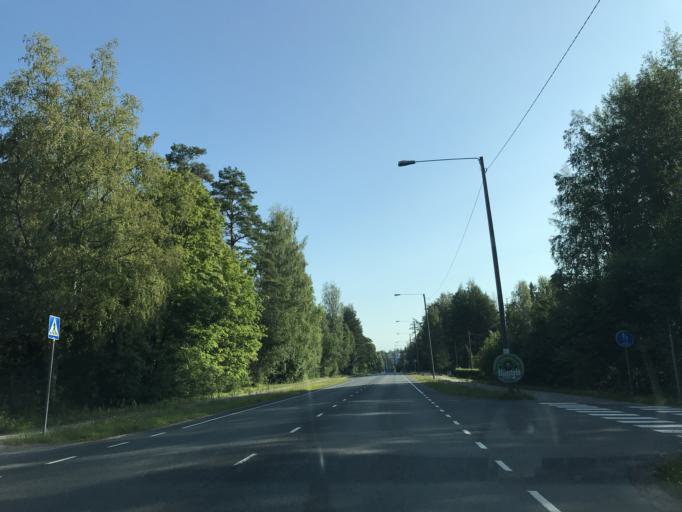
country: FI
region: Paijanne Tavastia
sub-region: Lahti
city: Orimattila
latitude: 60.7979
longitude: 25.7245
